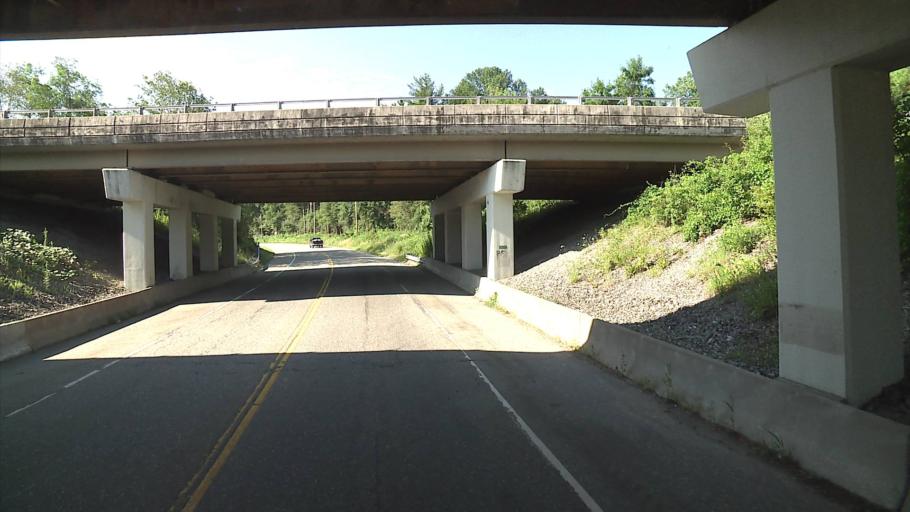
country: US
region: Connecticut
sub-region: New London County
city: Montville Center
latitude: 41.5623
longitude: -72.1650
